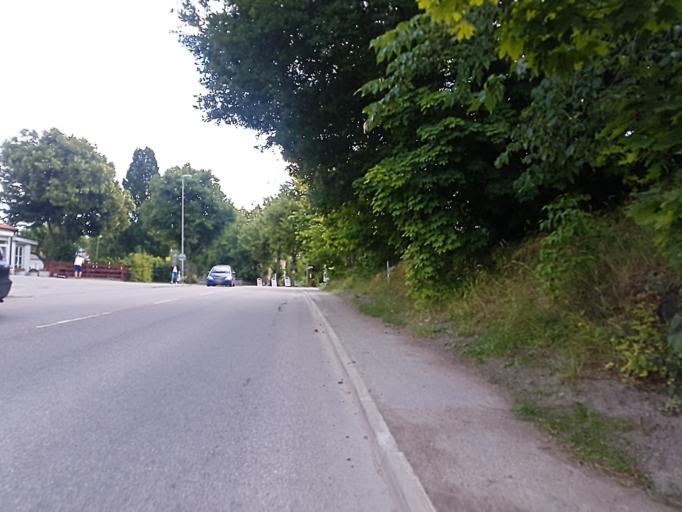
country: SE
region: Soedermanland
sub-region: Gnesta Kommun
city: Gnesta
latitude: 59.0492
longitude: 17.3035
